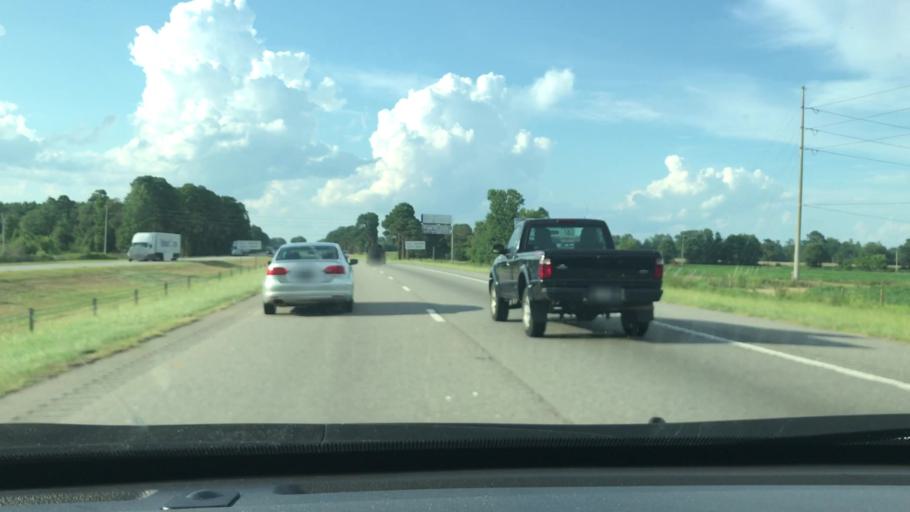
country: US
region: North Carolina
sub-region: Robeson County
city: Lumberton
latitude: 34.6925
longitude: -78.9986
